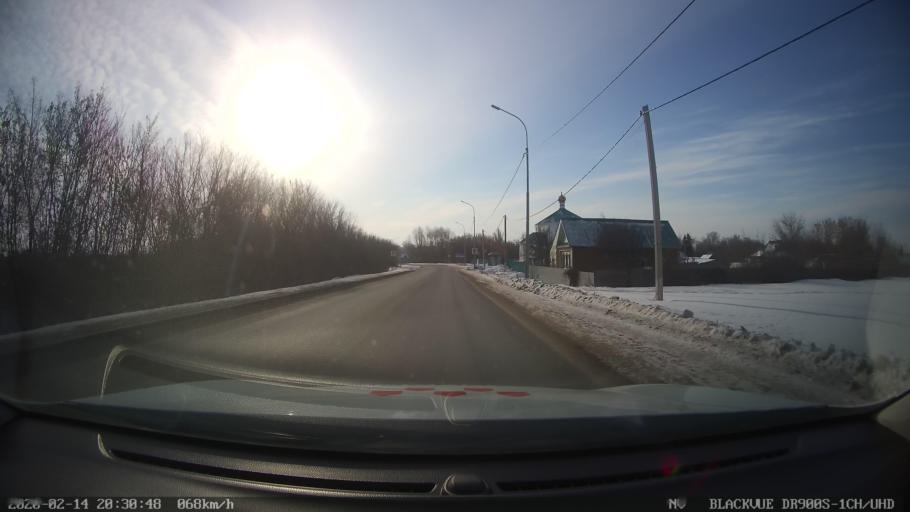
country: RU
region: Tatarstan
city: Stolbishchi
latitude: 55.4401
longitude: 48.9919
